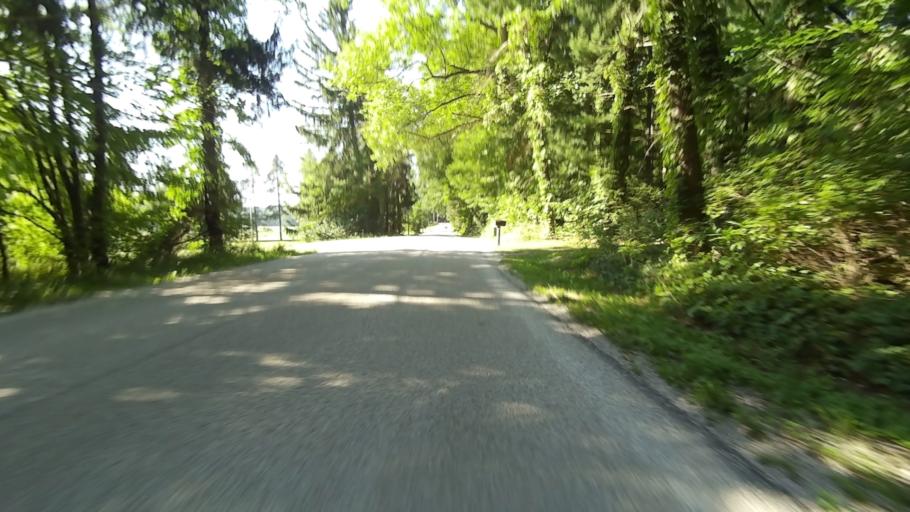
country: US
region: Ohio
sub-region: Portage County
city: Mantua
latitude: 41.2671
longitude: -81.2773
